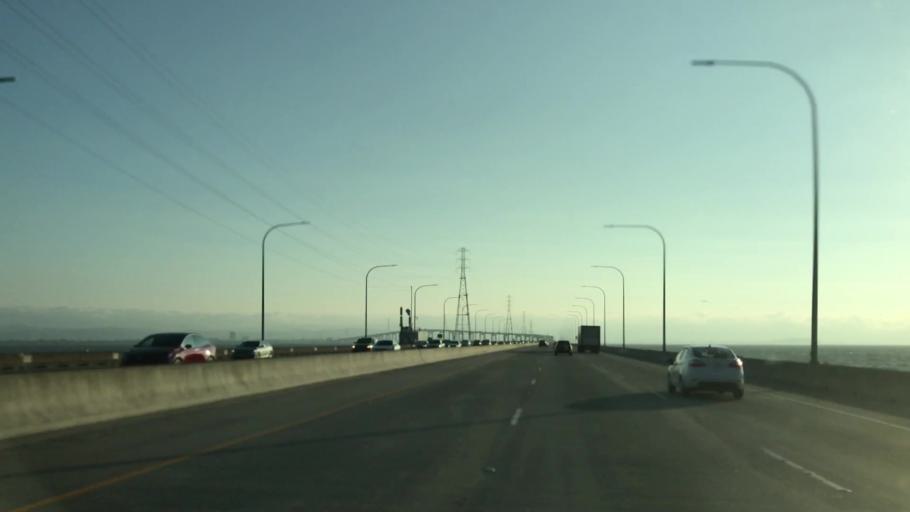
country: US
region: California
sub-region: San Mateo County
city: Foster City
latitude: 37.5984
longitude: -122.2193
